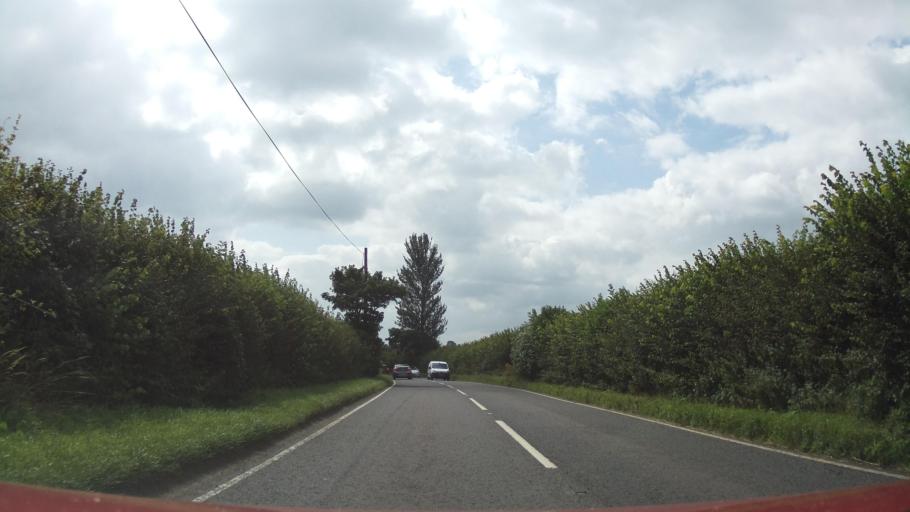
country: GB
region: England
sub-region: Dorset
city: Stalbridge
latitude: 50.9924
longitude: -2.4103
